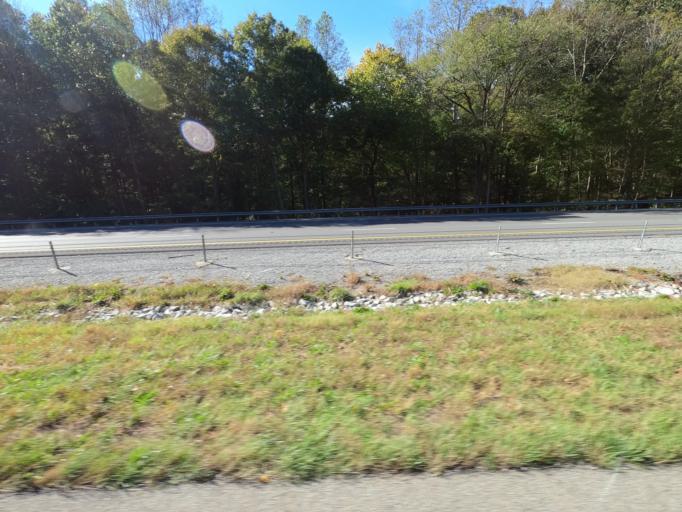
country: US
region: Tennessee
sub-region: Dickson County
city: White Bluff
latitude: 36.0269
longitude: -87.1983
